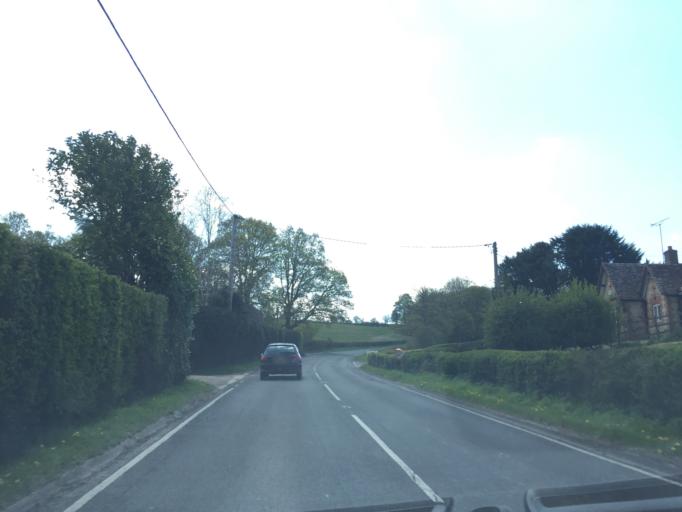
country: GB
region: England
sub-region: Kent
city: Edenbridge
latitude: 51.1430
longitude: 0.1074
